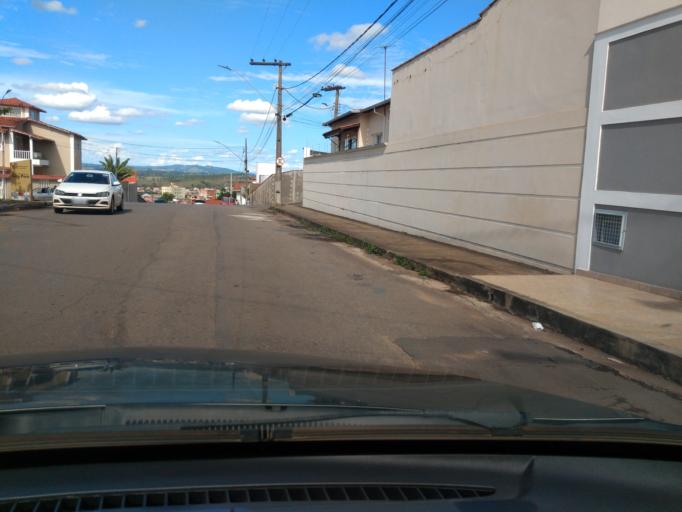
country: BR
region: Minas Gerais
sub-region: Tres Coracoes
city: Tres Coracoes
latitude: -21.6875
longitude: -45.2627
